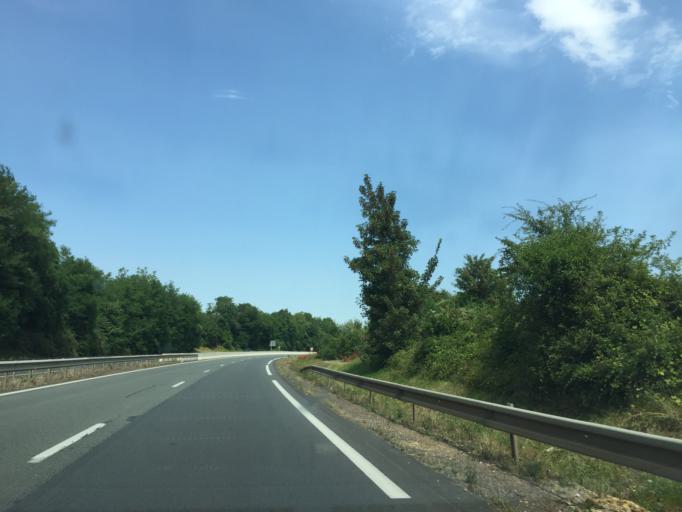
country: FR
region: Poitou-Charentes
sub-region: Departement de la Vienne
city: Biard
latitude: 46.5624
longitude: 0.3028
